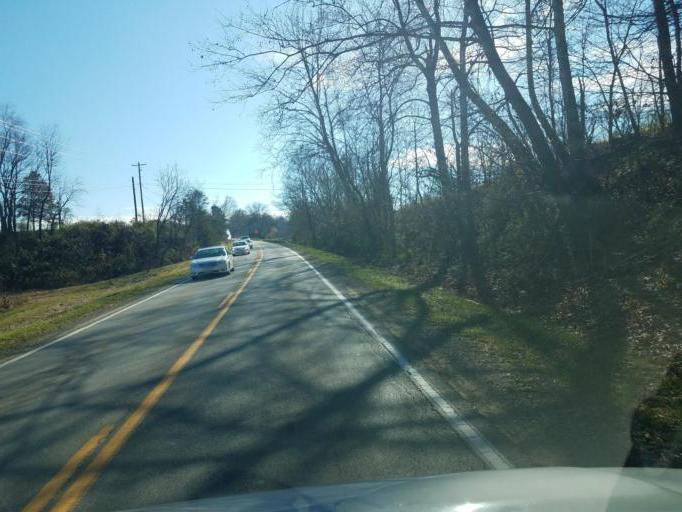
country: US
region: Ohio
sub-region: Scioto County
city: Sciotodale
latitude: 38.8499
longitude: -82.8557
